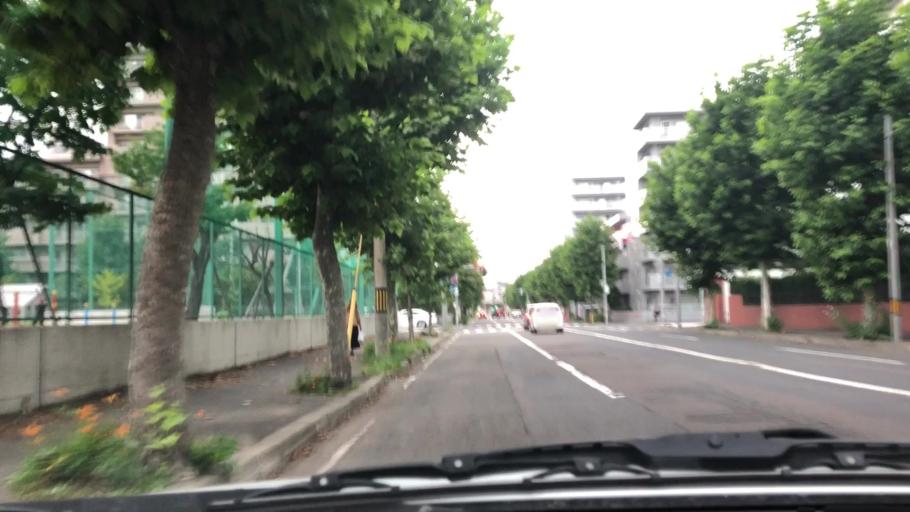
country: JP
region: Hokkaido
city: Sapporo
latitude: 43.0680
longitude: 141.3292
